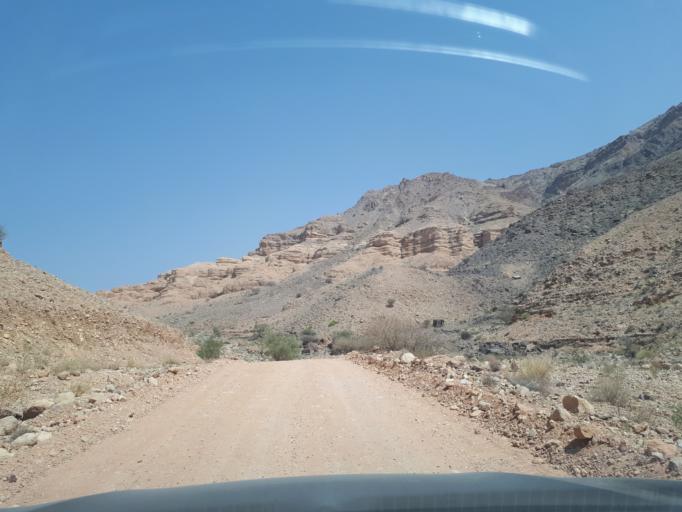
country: OM
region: Ash Sharqiyah
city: Ibra'
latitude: 23.0746
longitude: 58.8809
